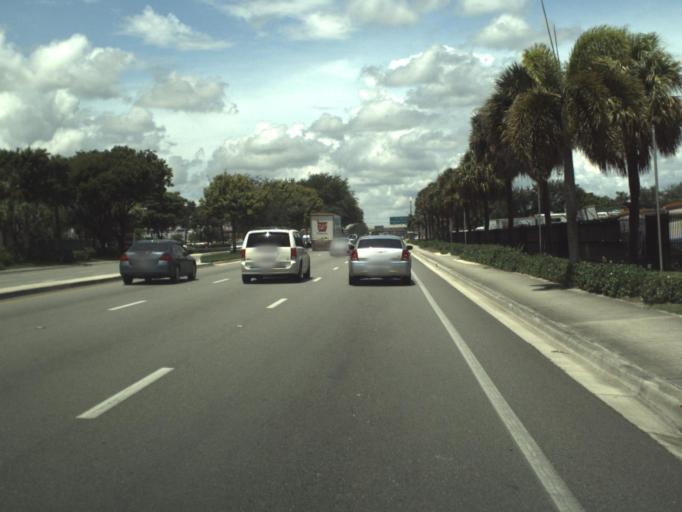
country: US
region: Florida
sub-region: Palm Beach County
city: Mangonia Park
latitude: 26.7831
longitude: -80.0927
